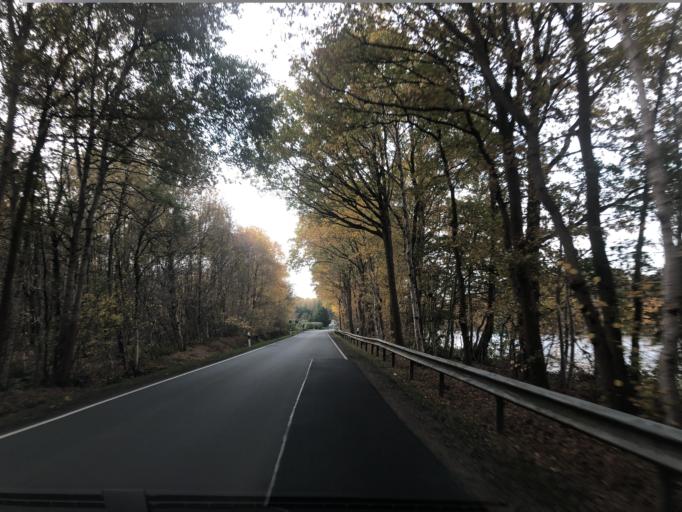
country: DE
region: Lower Saxony
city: Edewecht
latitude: 53.0855
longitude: 7.9493
